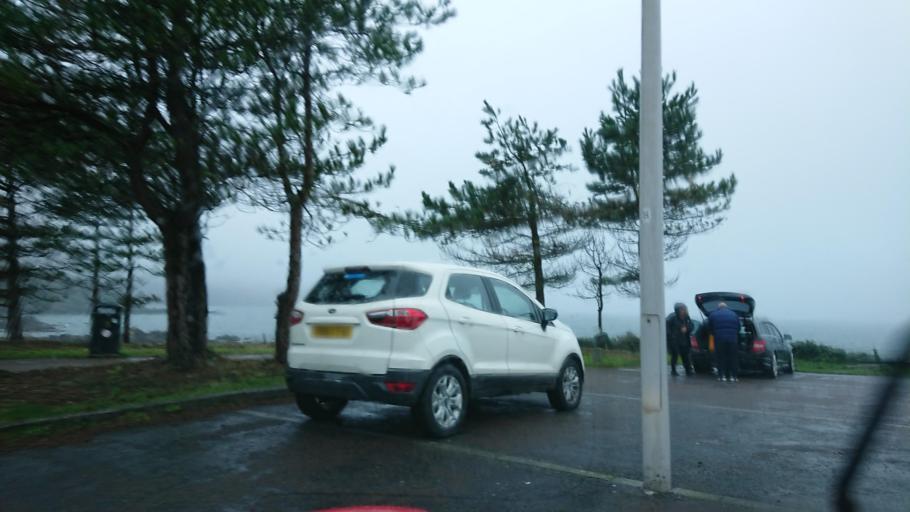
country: GB
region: England
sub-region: Plymouth
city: Plymouth
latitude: 50.3586
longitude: -4.1277
